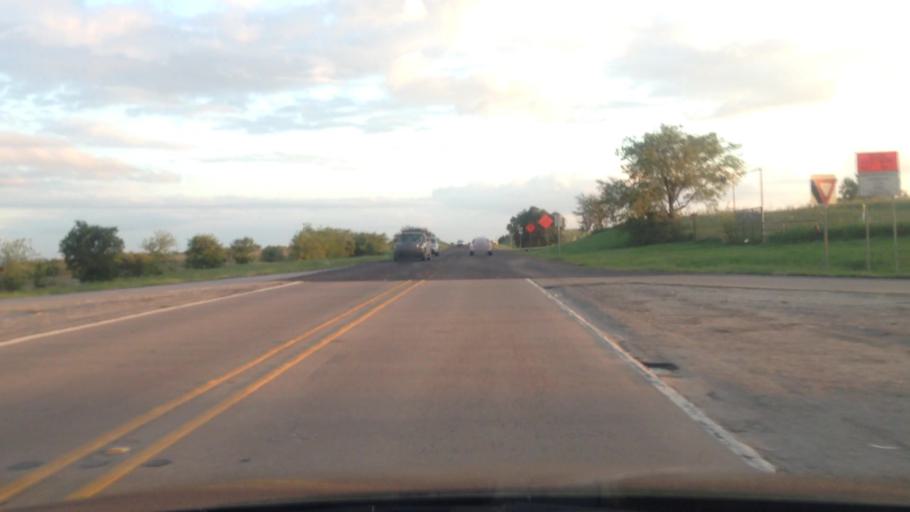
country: US
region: Texas
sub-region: Tarrant County
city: Benbrook
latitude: 32.6918
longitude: -97.4991
